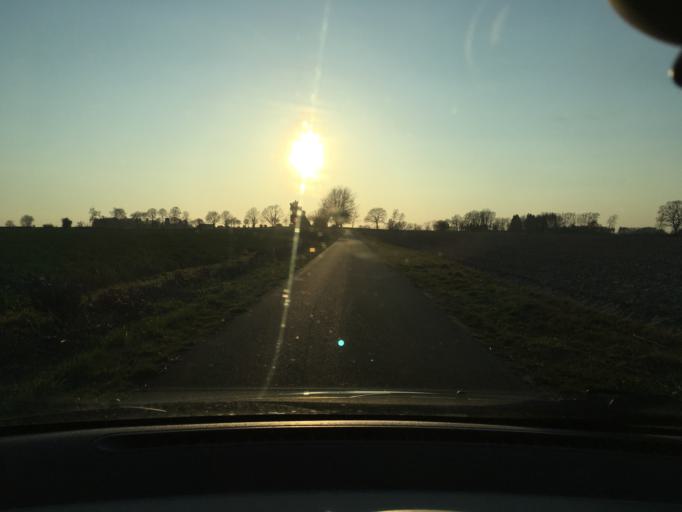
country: DE
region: Lower Saxony
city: Altenmedingen
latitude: 53.1491
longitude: 10.6454
